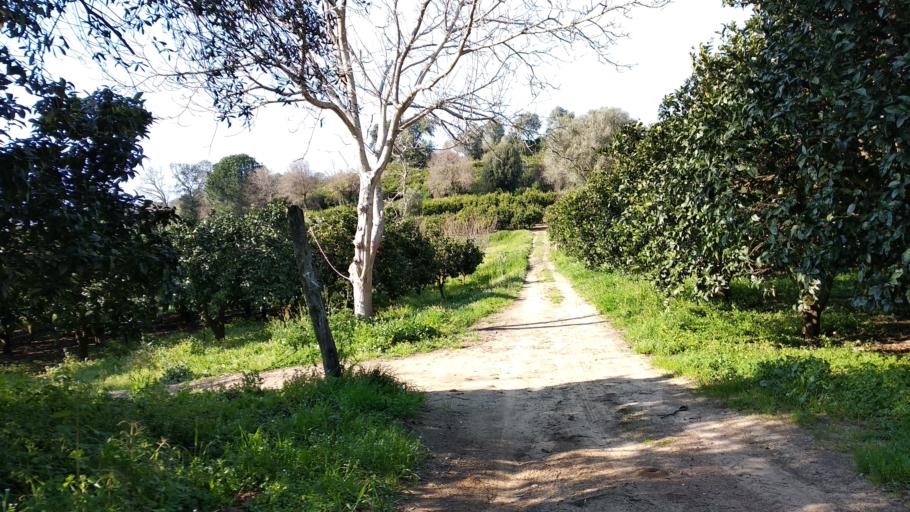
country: IT
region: Calabria
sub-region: Provincia di Reggio Calabria
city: Rizziconi
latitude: 38.4302
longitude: 15.9595
